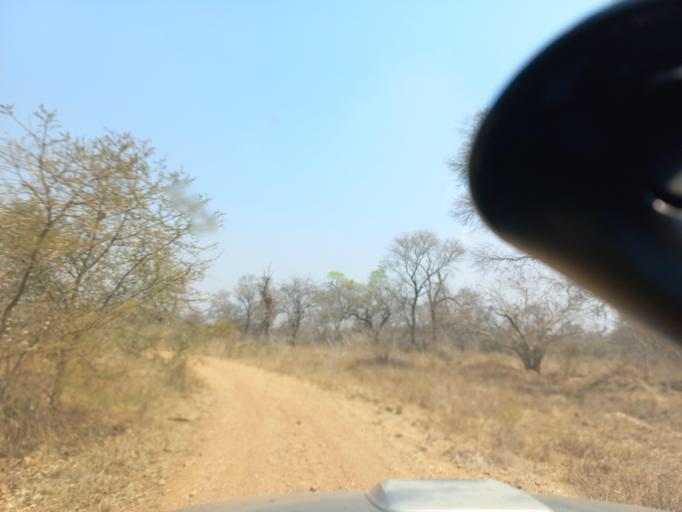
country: ZW
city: Chirundu
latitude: -15.9327
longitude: 28.7208
